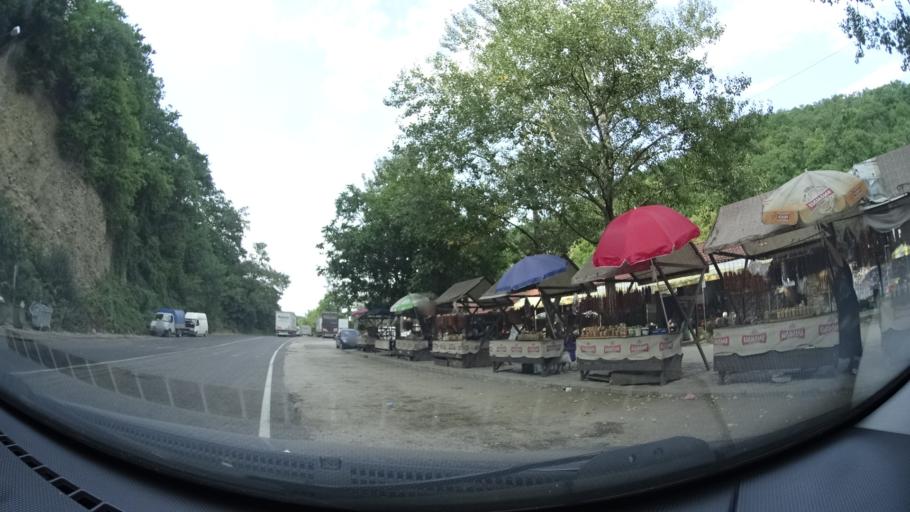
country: GE
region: Kakheti
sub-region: Gurjaani
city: Gurjaani
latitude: 41.6720
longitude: 45.8356
